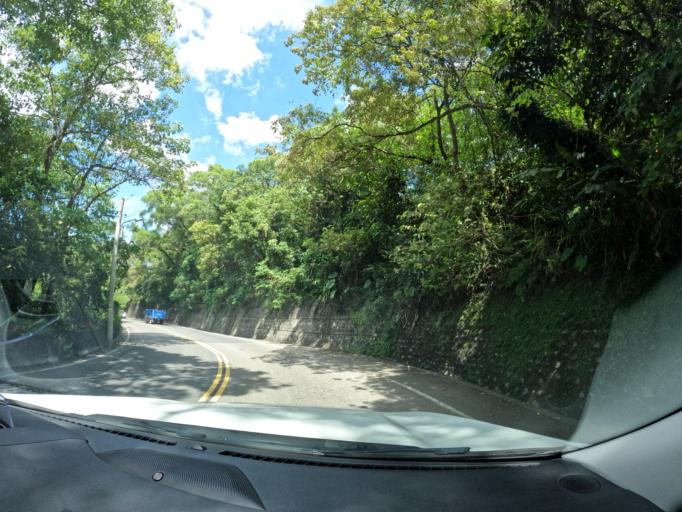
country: TW
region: Taipei
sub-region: Taipei
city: Banqiao
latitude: 25.1154
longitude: 121.3876
